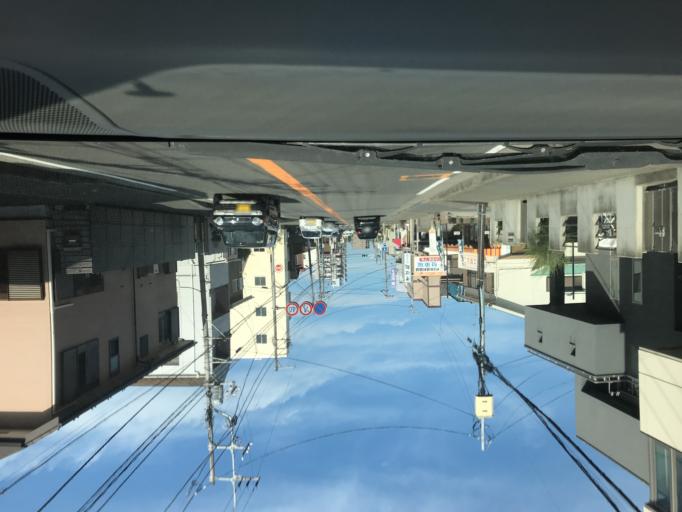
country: JP
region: Kanagawa
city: Fujisawa
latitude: 35.3416
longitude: 139.4583
